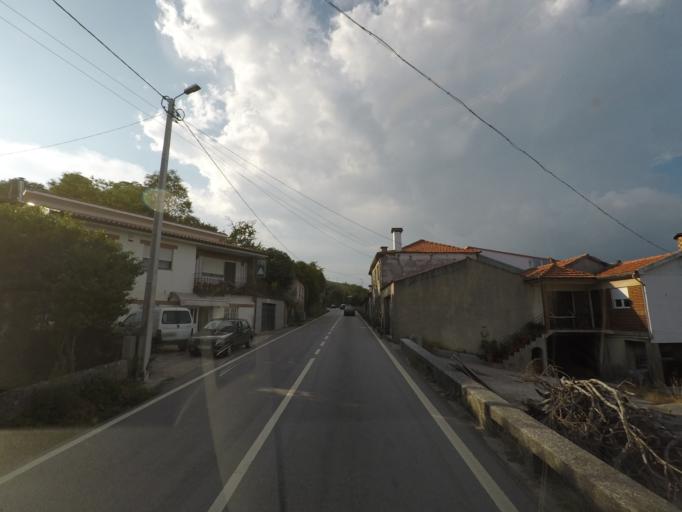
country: PT
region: Porto
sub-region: Baiao
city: Valadares
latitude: 41.1886
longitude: -7.9426
